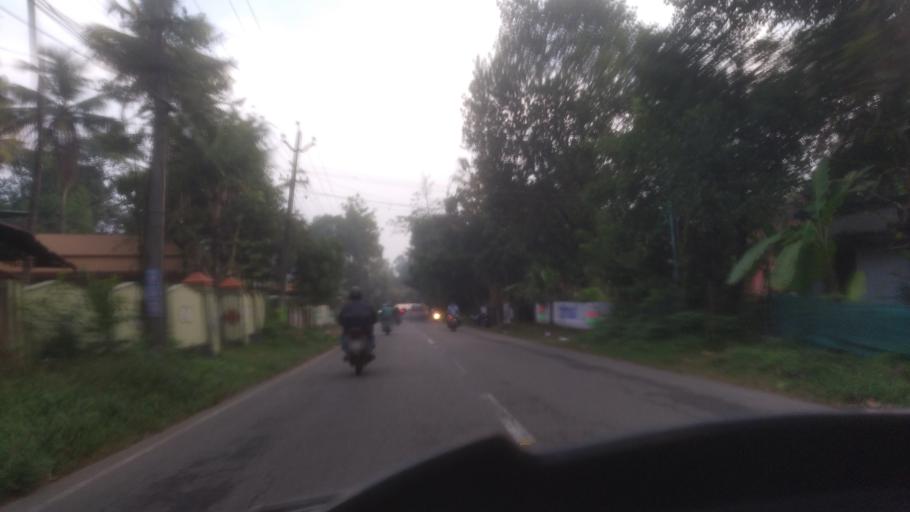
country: IN
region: Kerala
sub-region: Ernakulam
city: Perumbavoor
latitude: 10.1140
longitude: 76.4292
